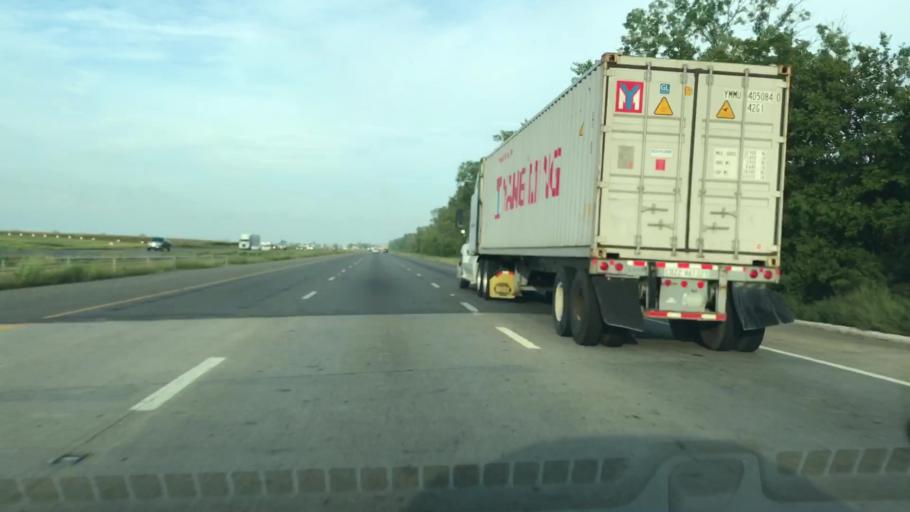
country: US
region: Ohio
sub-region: Madison County
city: Choctaw Lake
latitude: 39.9474
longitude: -83.4181
